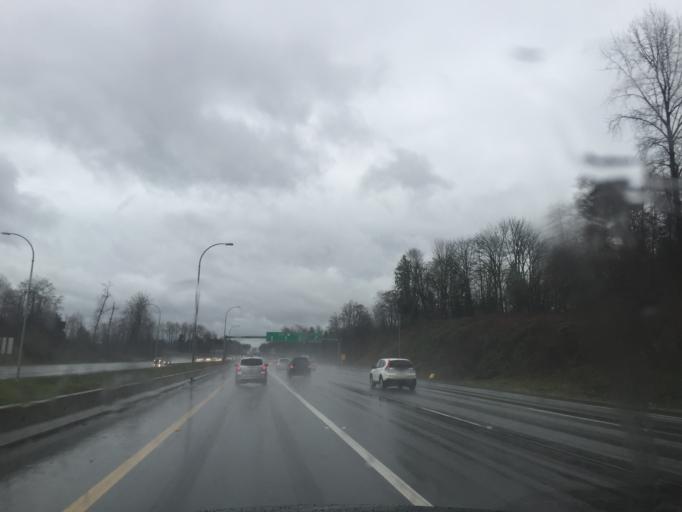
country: CA
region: British Columbia
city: Pitt Meadows
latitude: 49.1722
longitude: -122.6999
